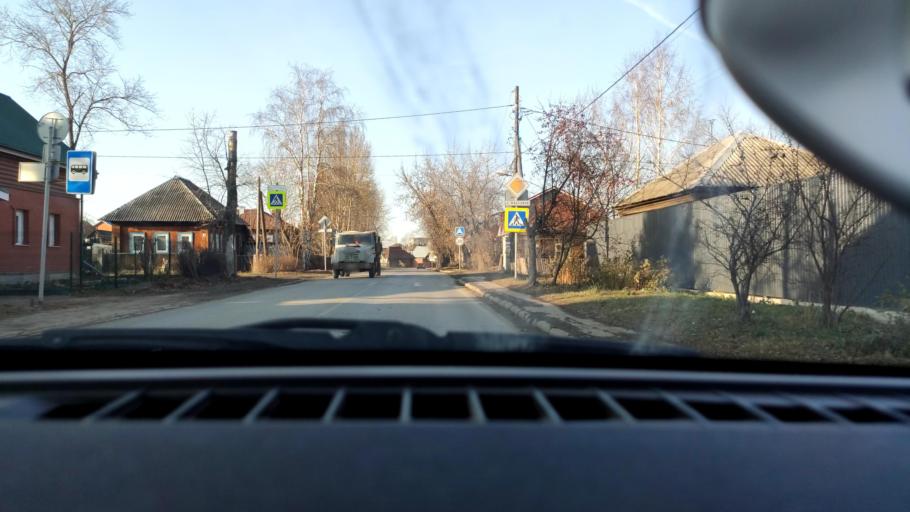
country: RU
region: Perm
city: Perm
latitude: 58.0165
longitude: 56.3154
